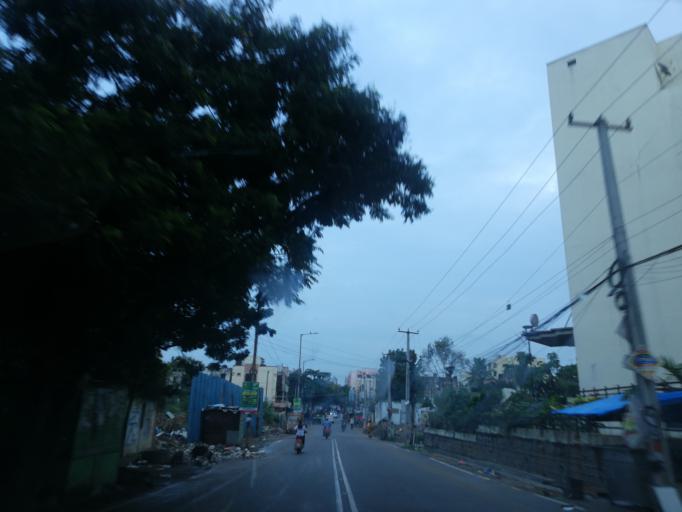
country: IN
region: Telangana
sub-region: Rangareddi
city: Kukatpalli
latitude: 17.4836
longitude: 78.3932
